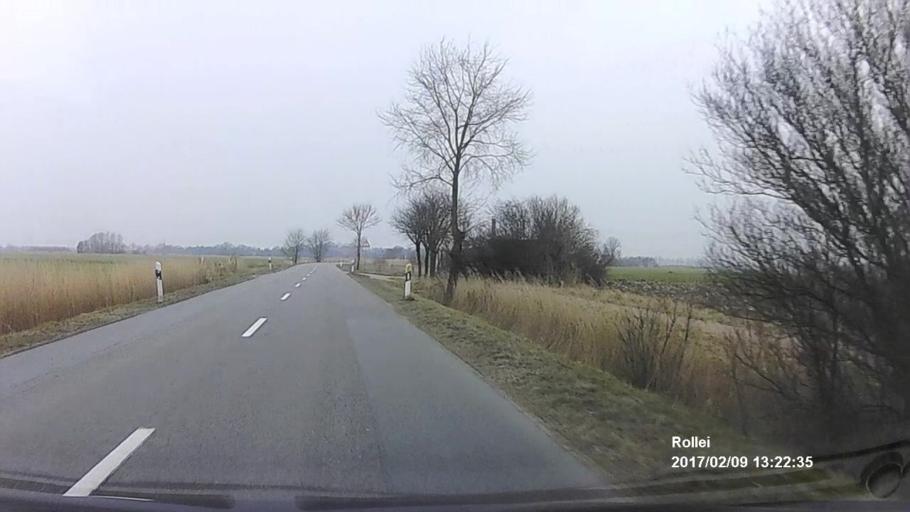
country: DE
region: Lower Saxony
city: Hinte
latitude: 53.4569
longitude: 7.1482
